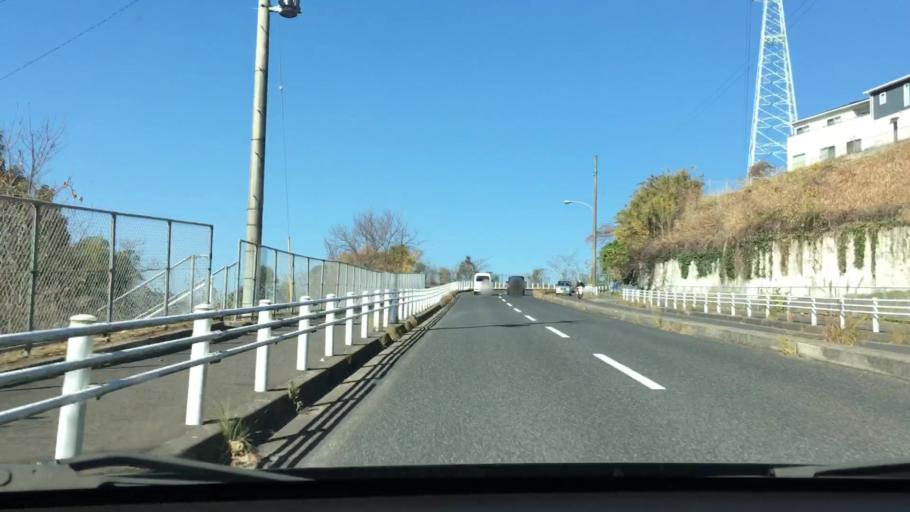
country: JP
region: Kagoshima
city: Kagoshima-shi
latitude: 31.5553
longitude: 130.5271
